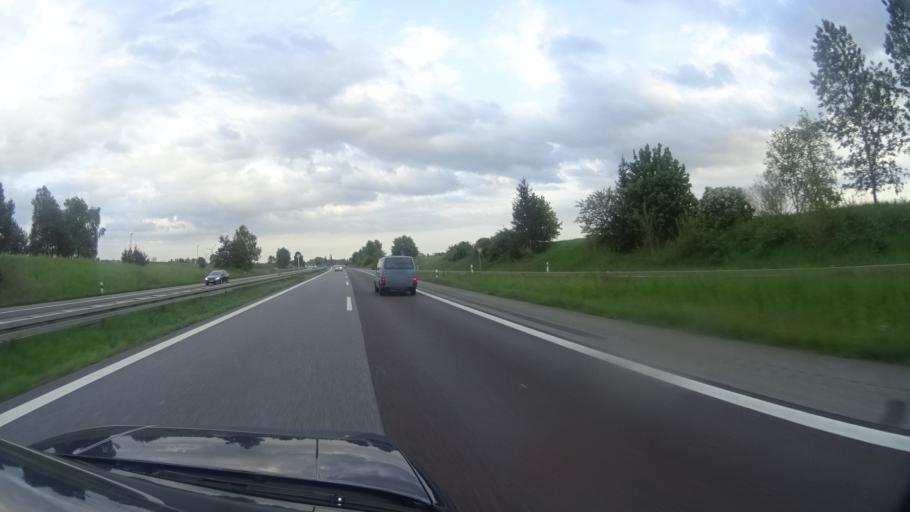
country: DE
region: Brandenburg
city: Walsleben
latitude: 52.9489
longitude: 12.6631
